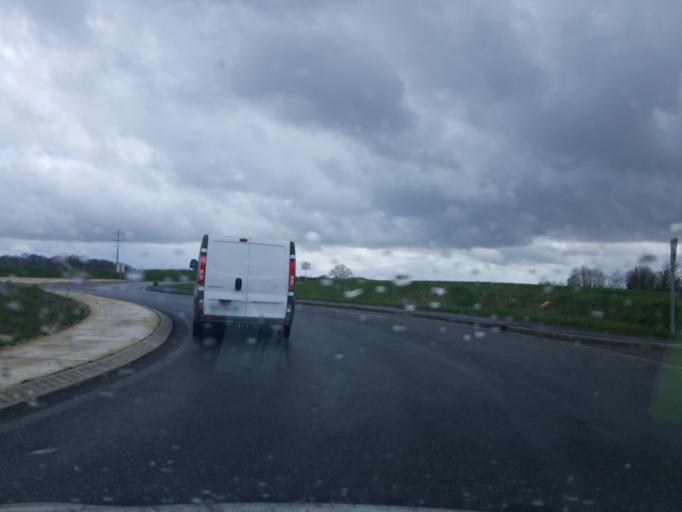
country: FR
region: Picardie
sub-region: Departement de l'Oise
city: Trie-Chateau
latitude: 49.2817
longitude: 1.8347
